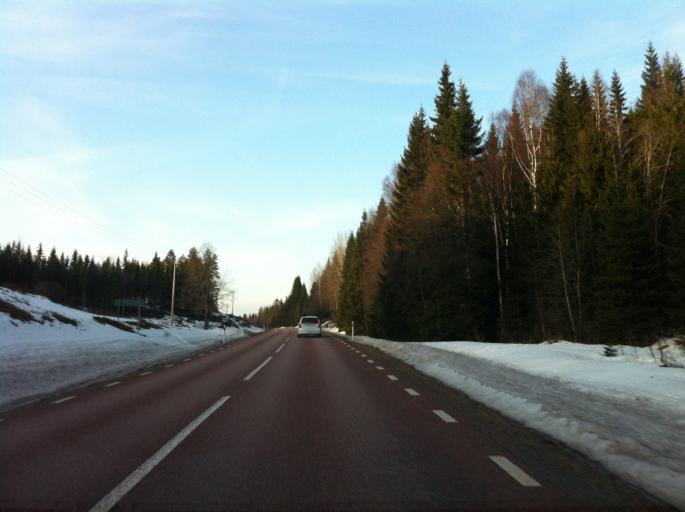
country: SE
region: Dalarna
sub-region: Vansbro Kommun
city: Vansbro
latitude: 60.2634
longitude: 14.1725
